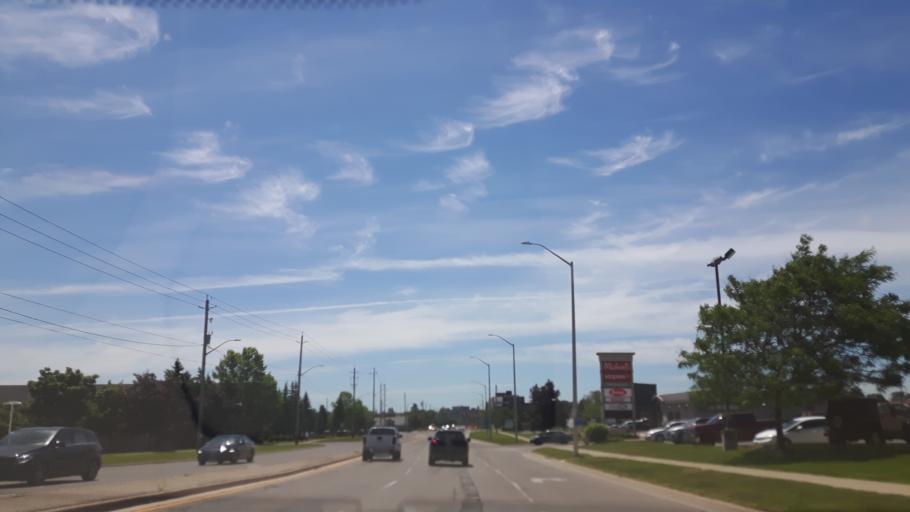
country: CA
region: Ontario
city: London
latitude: 43.0291
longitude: -81.2841
